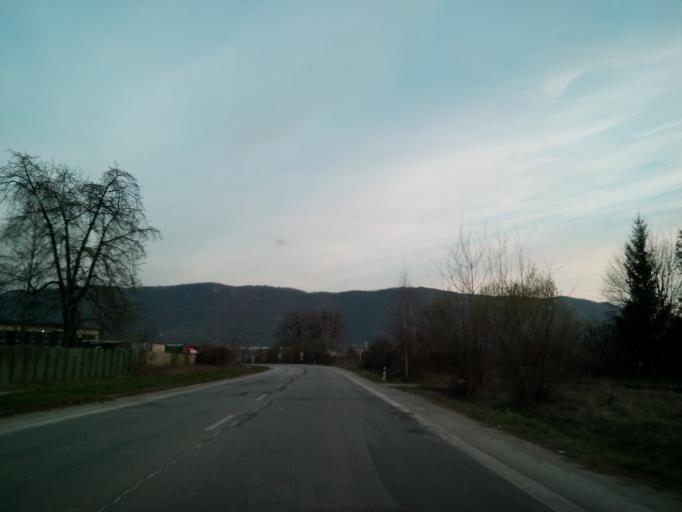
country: SK
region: Kosicky
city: Roznava
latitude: 48.6491
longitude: 20.5225
